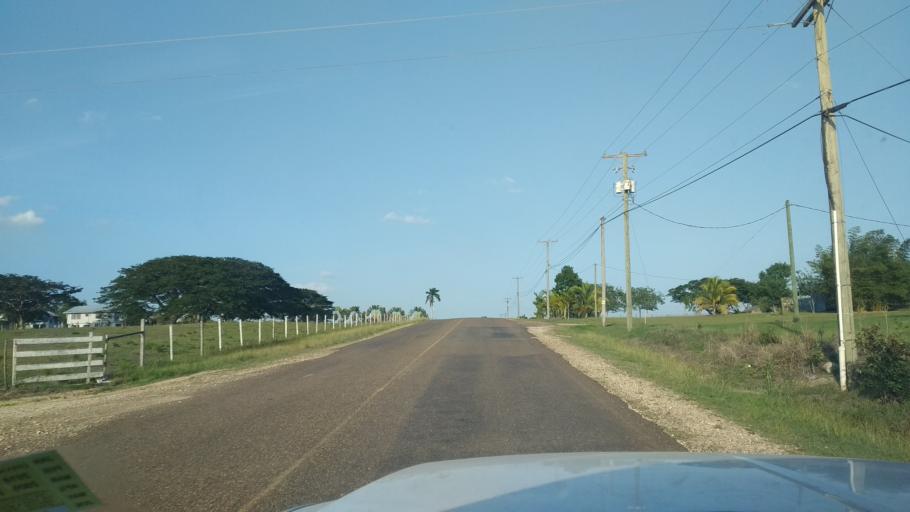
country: BZ
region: Cayo
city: San Ignacio
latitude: 17.2566
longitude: -88.9920
